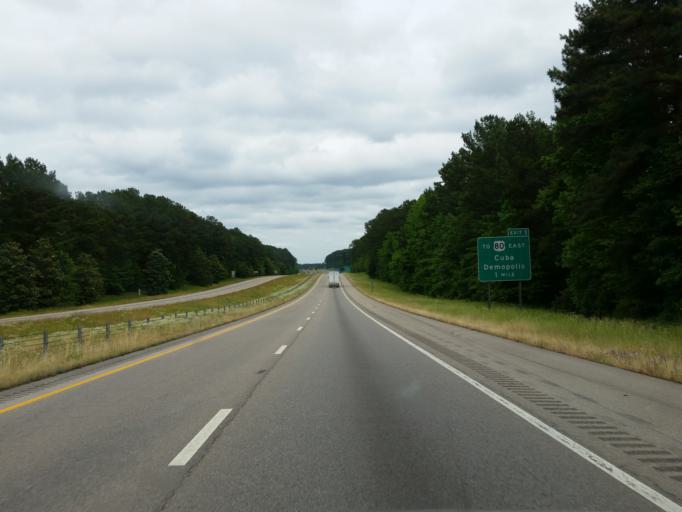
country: US
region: Alabama
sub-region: Sumter County
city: York
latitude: 32.4466
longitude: -88.4107
